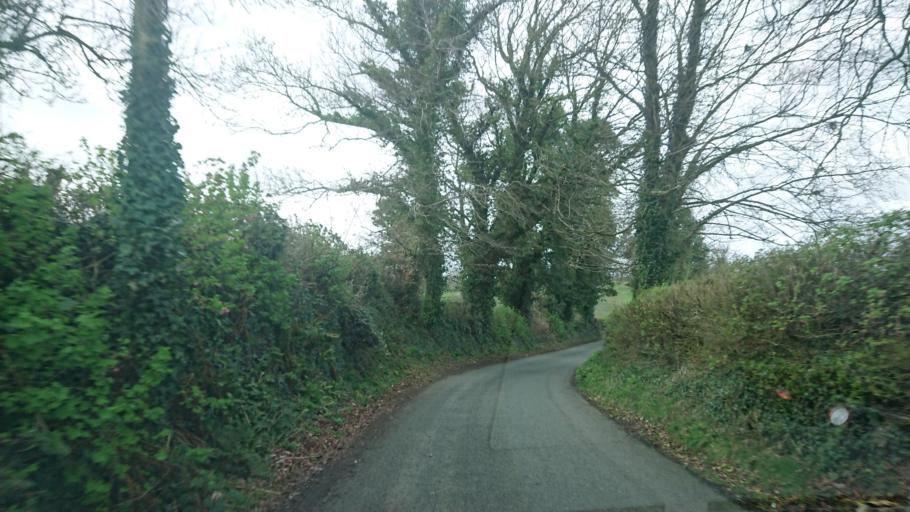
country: IE
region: Leinster
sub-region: Kildare
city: Eadestown
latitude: 53.1650
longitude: -6.6095
